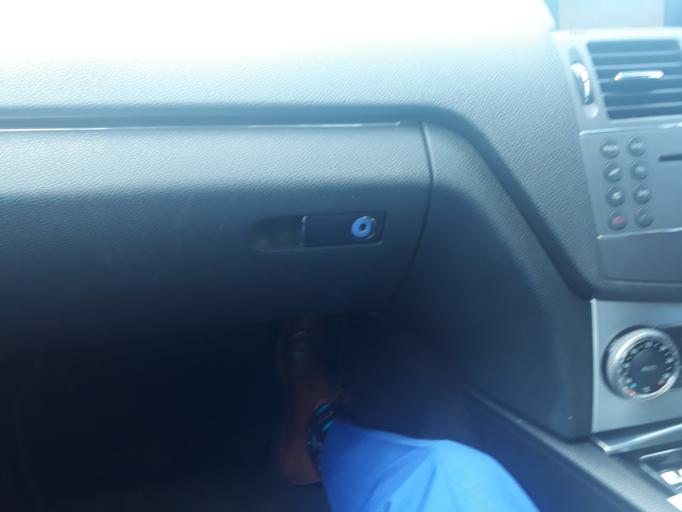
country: BW
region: South East
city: Gaborone
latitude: -24.6735
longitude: 25.8918
